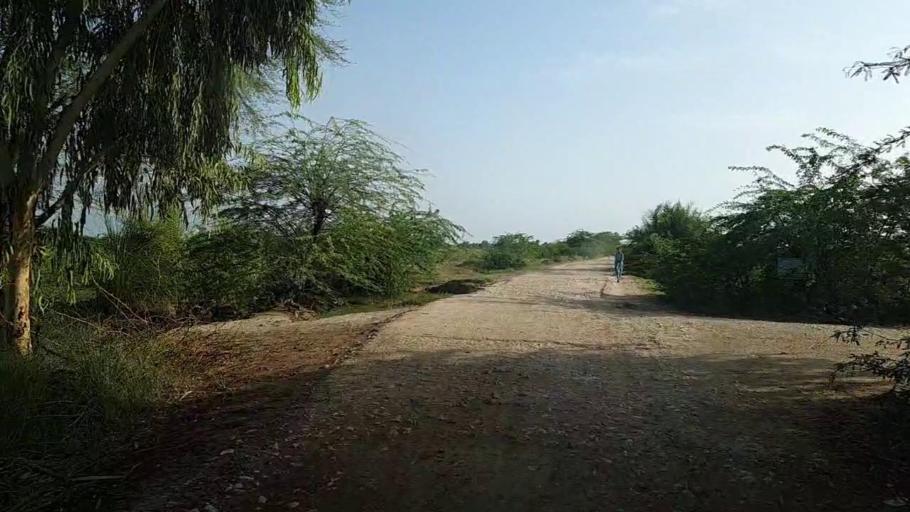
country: PK
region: Sindh
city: Pad Idan
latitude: 26.8161
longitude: 68.2377
